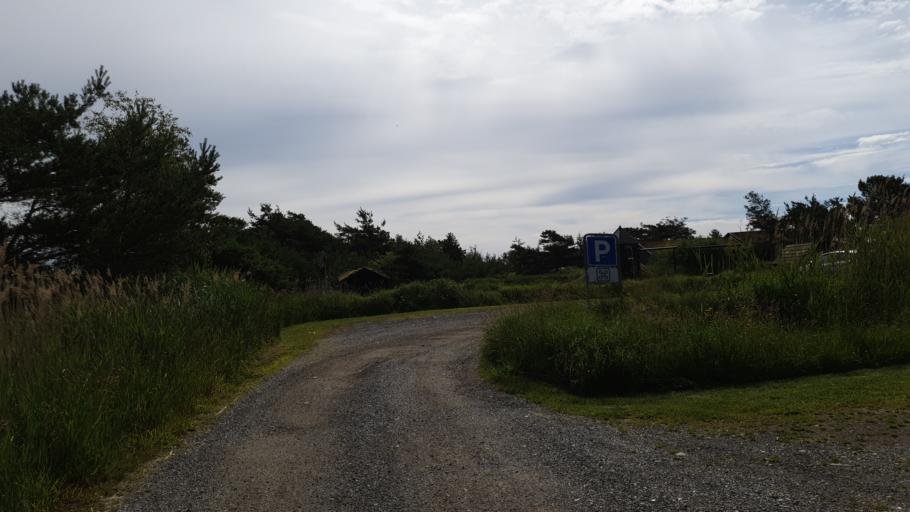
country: DK
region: North Denmark
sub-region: Laeso Kommune
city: Byrum
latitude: 57.2404
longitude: 10.9895
